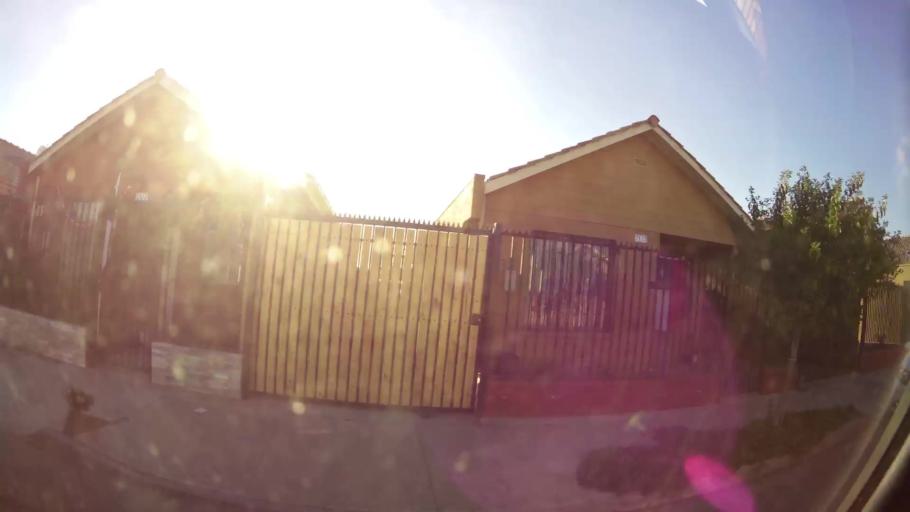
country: CL
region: Santiago Metropolitan
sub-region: Provincia de Talagante
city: Penaflor
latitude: -33.6002
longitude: -70.8578
